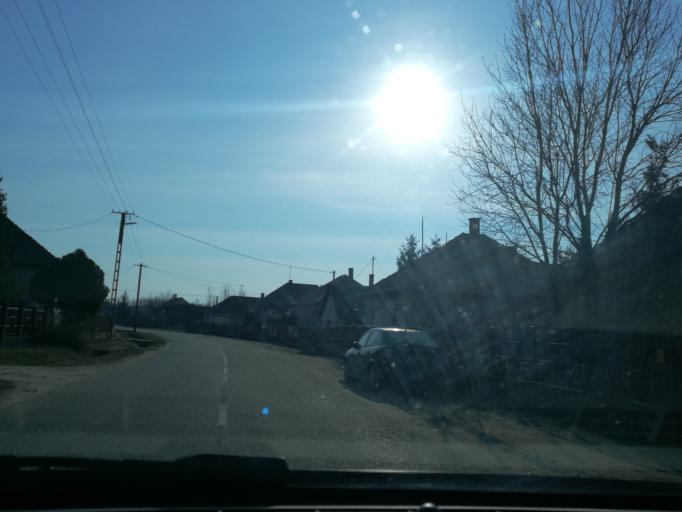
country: HU
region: Szabolcs-Szatmar-Bereg
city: Nyirbogdany
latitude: 48.0569
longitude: 21.9417
